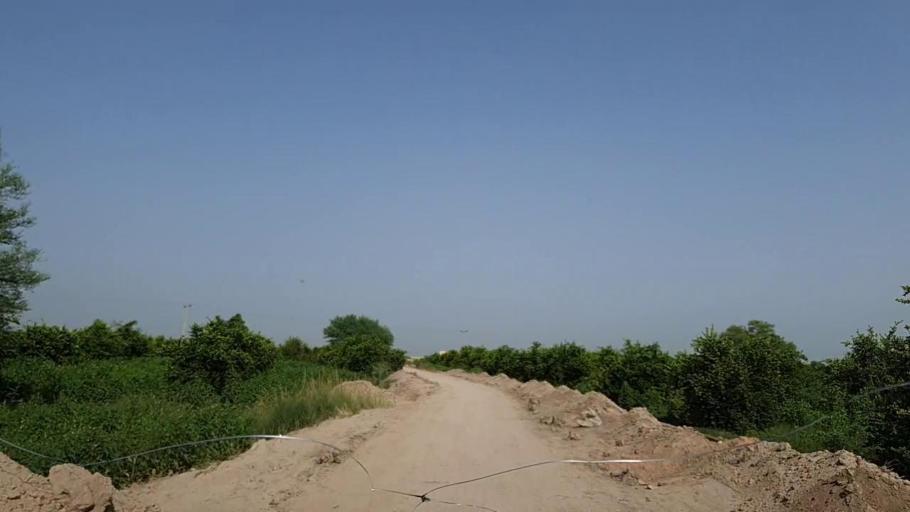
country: PK
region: Sindh
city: Kandiaro
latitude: 27.0729
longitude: 68.1376
